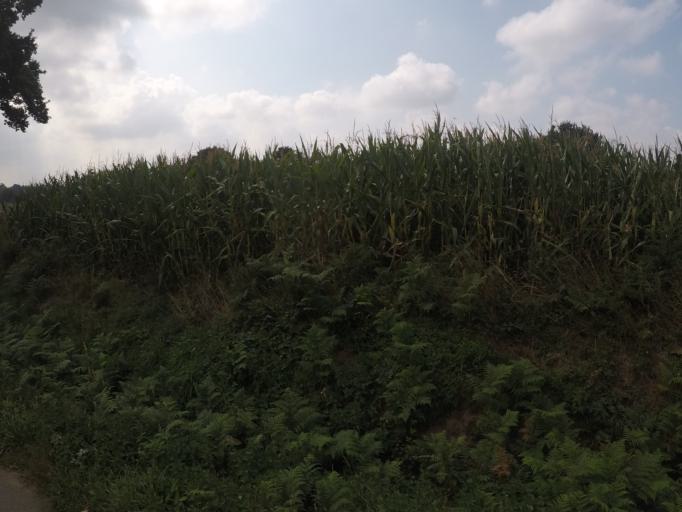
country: FR
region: Brittany
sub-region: Departement des Cotes-d'Armor
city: Plelo
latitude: 48.5615
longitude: -2.9530
